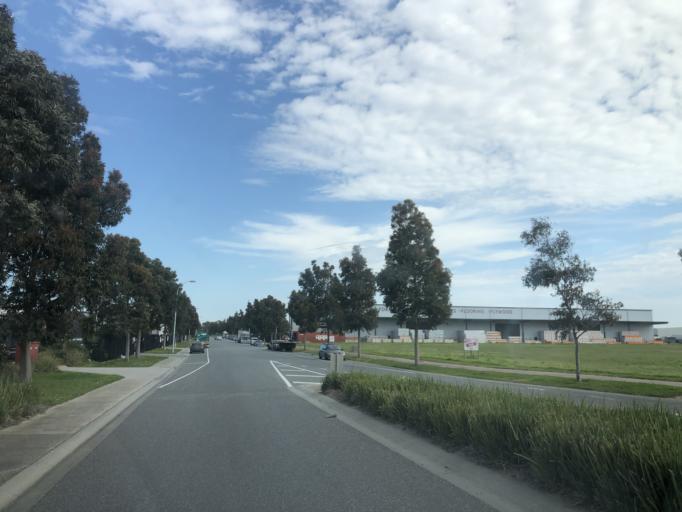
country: AU
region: Victoria
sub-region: Casey
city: Hampton Park
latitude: -38.0405
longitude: 145.2187
